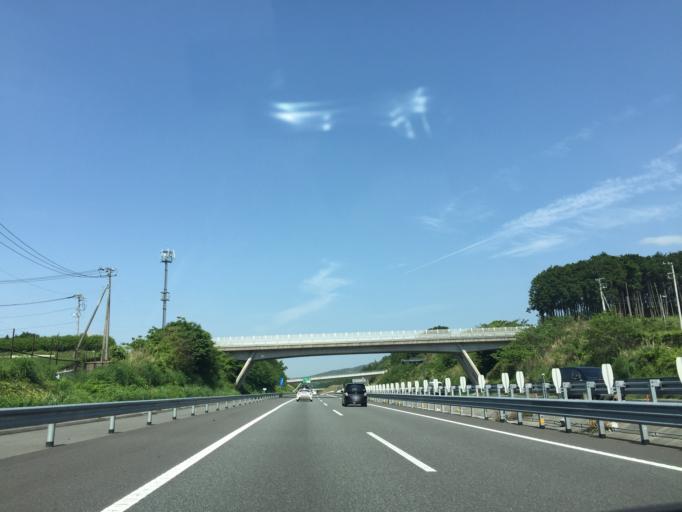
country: JP
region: Shizuoka
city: Numazu
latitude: 35.1528
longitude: 138.8407
